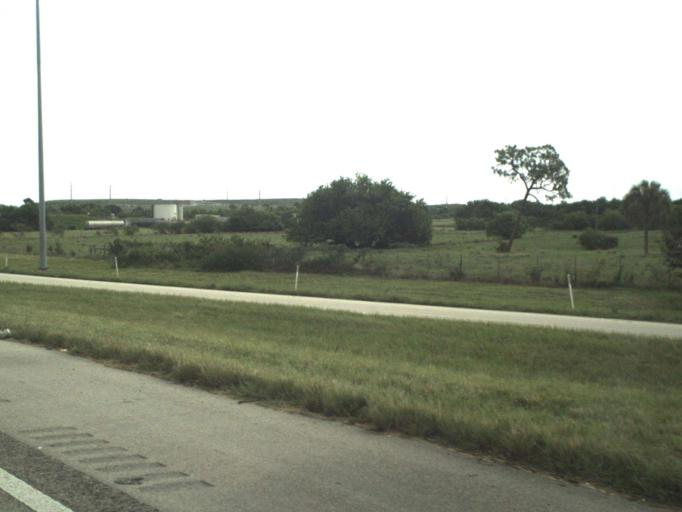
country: US
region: Florida
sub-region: Saint Lucie County
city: Fort Pierce South
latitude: 27.3779
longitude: -80.4073
